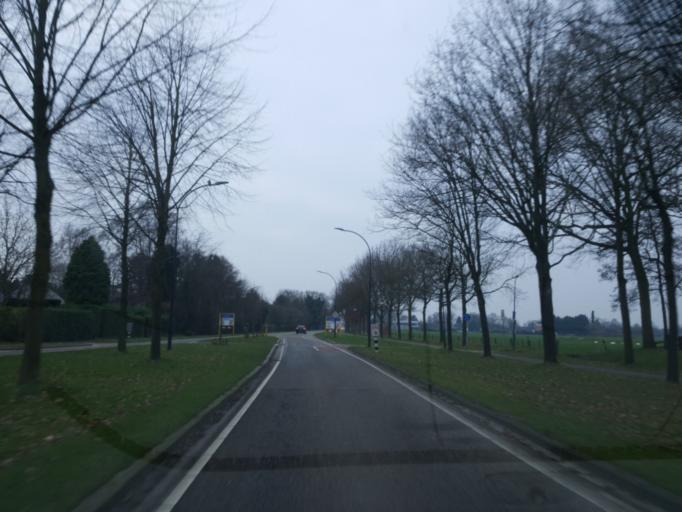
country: NL
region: North Holland
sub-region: Gemeente Wijdemeren
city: Nieuw-Loosdrecht
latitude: 52.2075
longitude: 5.1362
